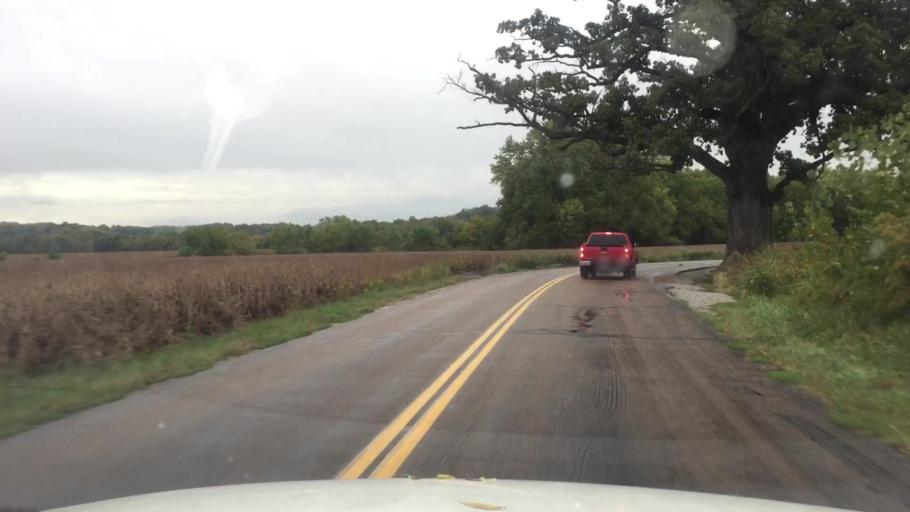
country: US
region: Missouri
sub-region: Boone County
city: Columbia
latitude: 38.8985
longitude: -92.4646
